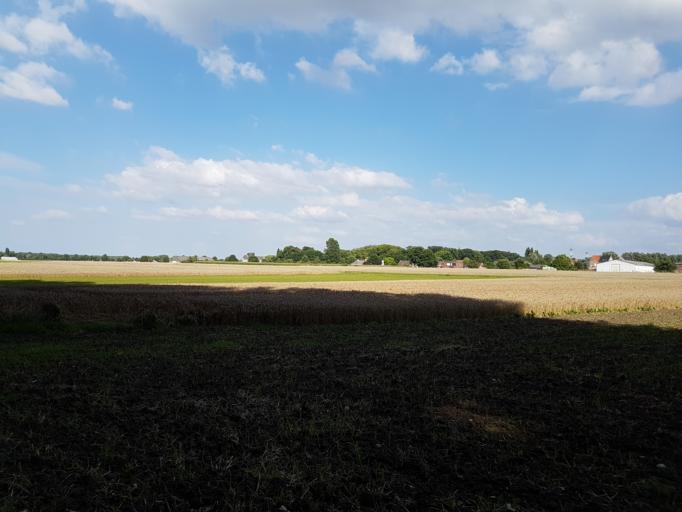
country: BE
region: Flanders
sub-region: Provincie Vlaams-Brabant
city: Steenokkerzeel
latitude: 50.9175
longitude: 4.4817
